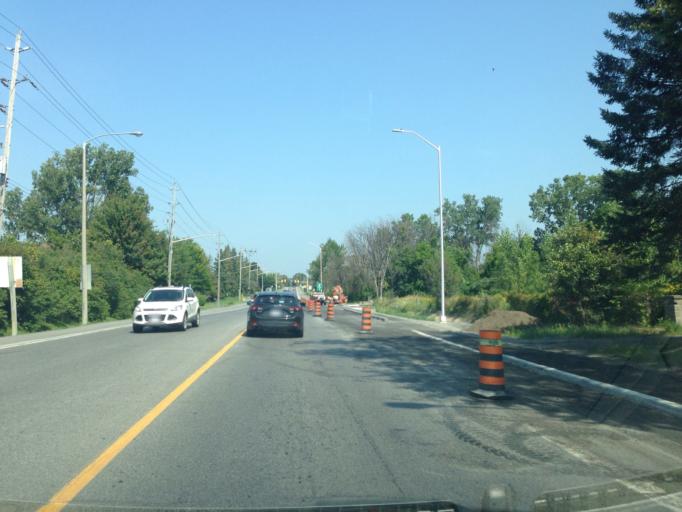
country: CA
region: Ontario
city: Ottawa
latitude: 45.4204
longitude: -75.5962
